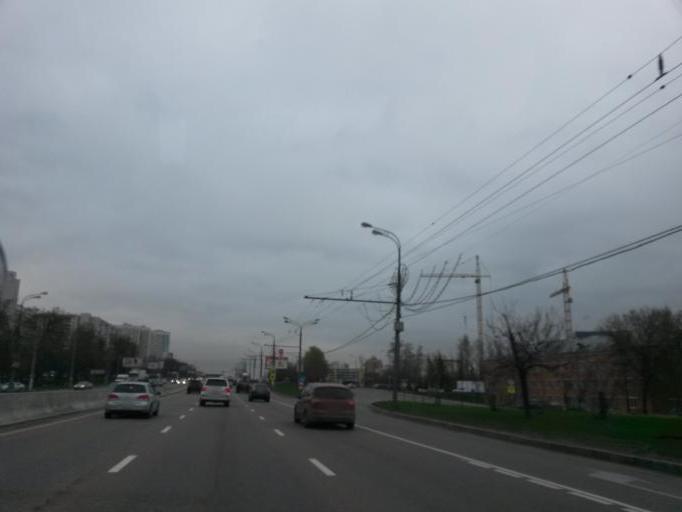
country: RU
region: Moscow
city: Annino
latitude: 55.5861
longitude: 37.5984
